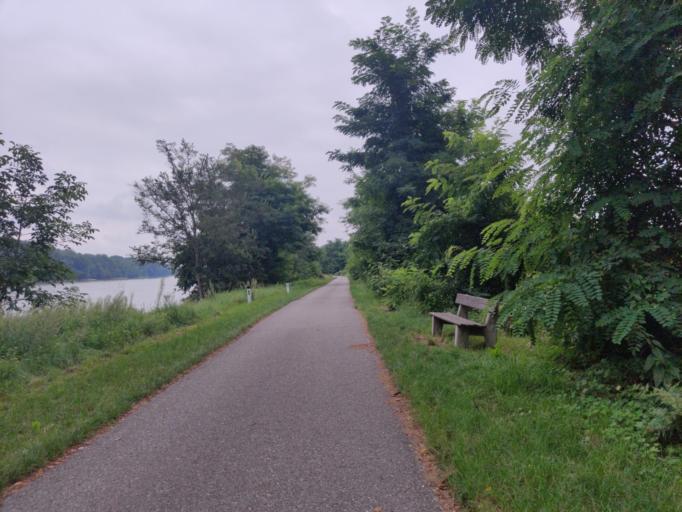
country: AT
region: Lower Austria
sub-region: Politischer Bezirk Tulln
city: Atzenbrugg
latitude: 48.3506
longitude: 15.9003
